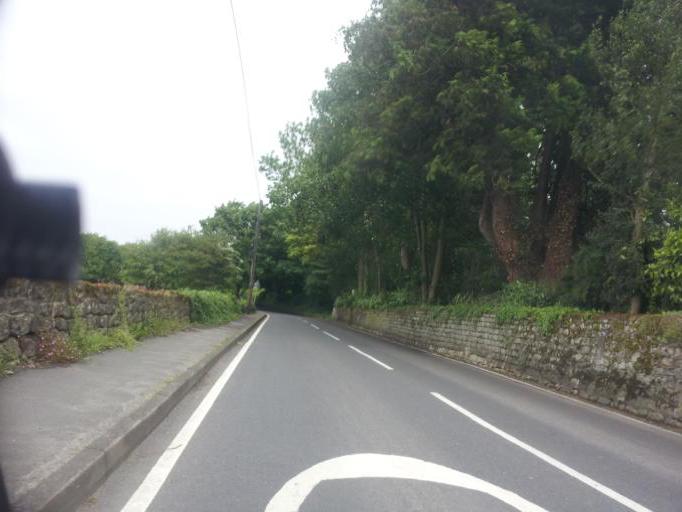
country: GB
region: England
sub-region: Kent
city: Wateringbury
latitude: 51.2543
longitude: 0.4704
